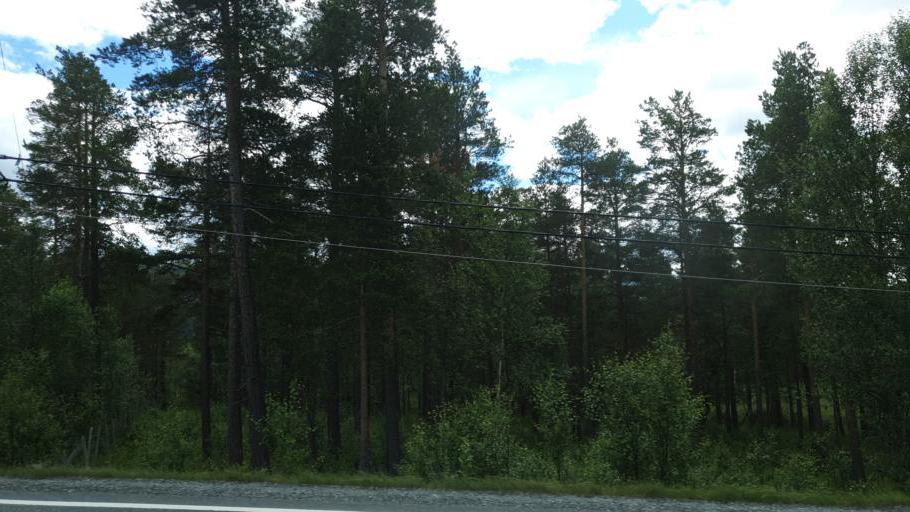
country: NO
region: Sor-Trondelag
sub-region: Oppdal
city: Oppdal
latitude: 62.6440
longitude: 9.8274
